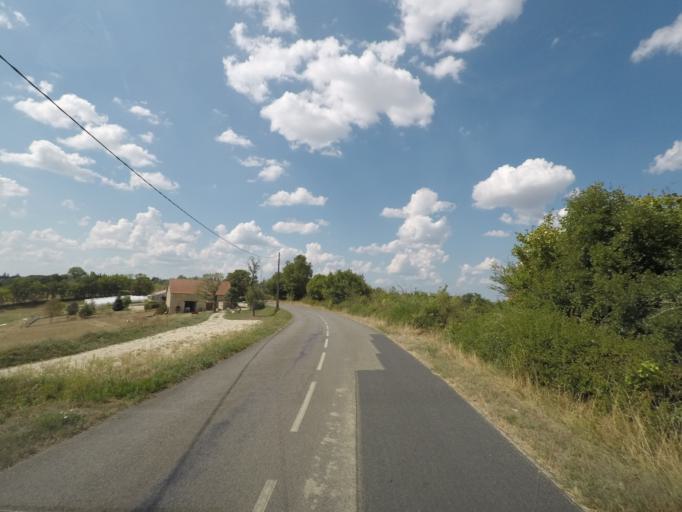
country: FR
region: Midi-Pyrenees
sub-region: Departement du Lot
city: Le Vigan
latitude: 44.6422
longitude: 1.5803
